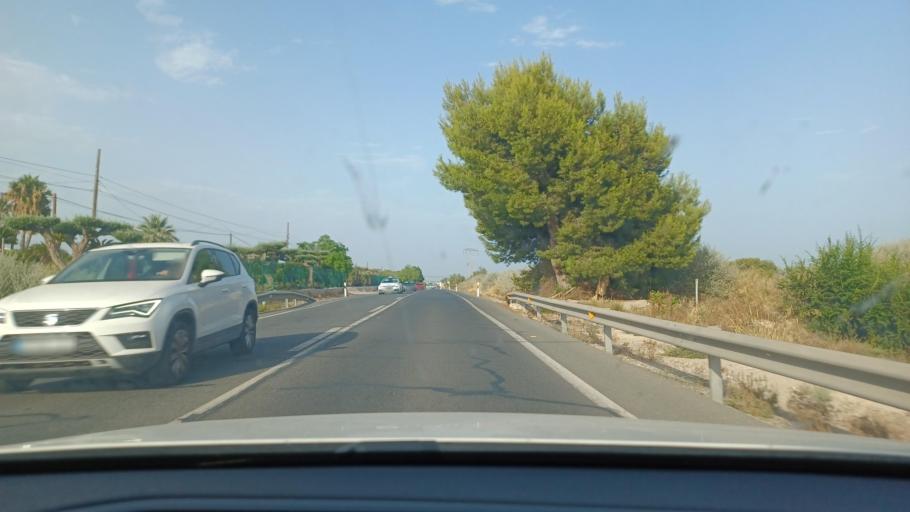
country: ES
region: Valencia
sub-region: Provincia de Alicante
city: Elche
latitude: 38.2818
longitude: -0.6340
